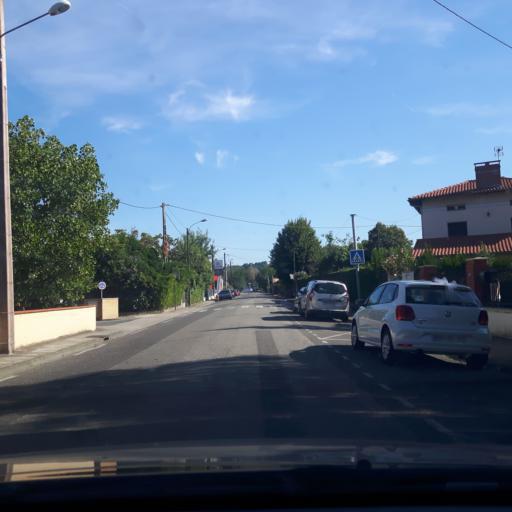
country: FR
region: Midi-Pyrenees
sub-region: Departement de la Haute-Garonne
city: Villemur-sur-Tarn
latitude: 43.8561
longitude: 1.4999
